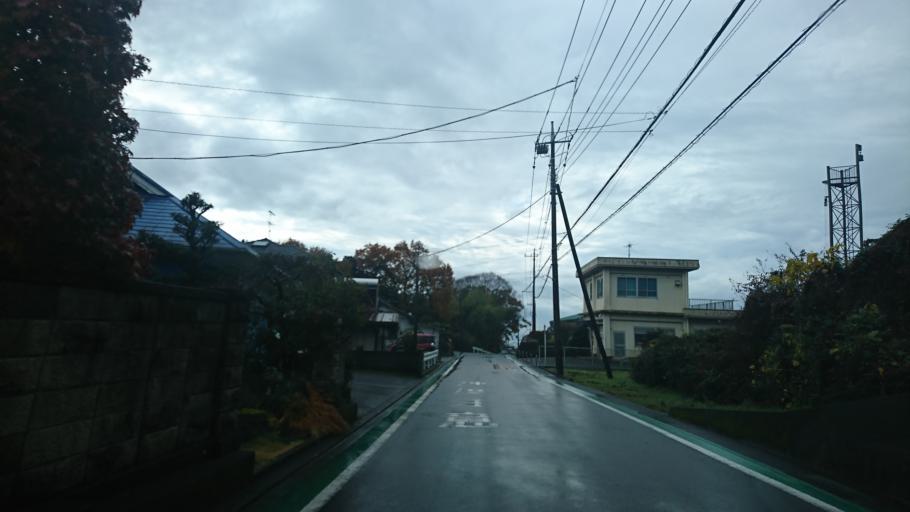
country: JP
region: Shizuoka
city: Fuji
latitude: 35.1967
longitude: 138.7269
